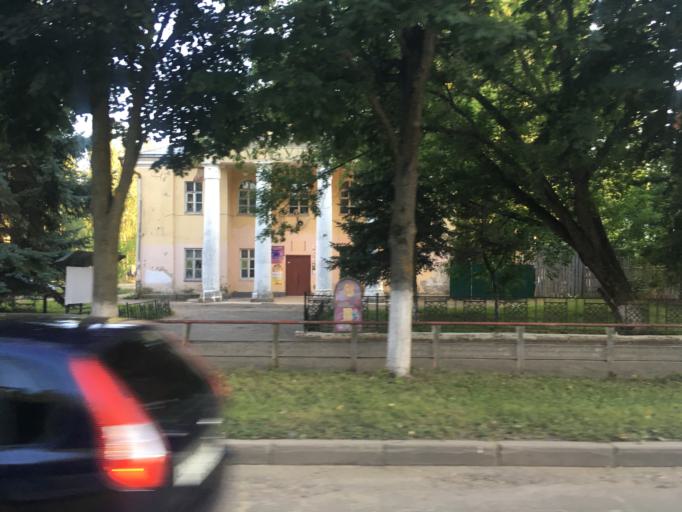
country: RU
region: Mariy-El
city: Yoshkar-Ola
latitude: 56.6460
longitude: 47.8907
